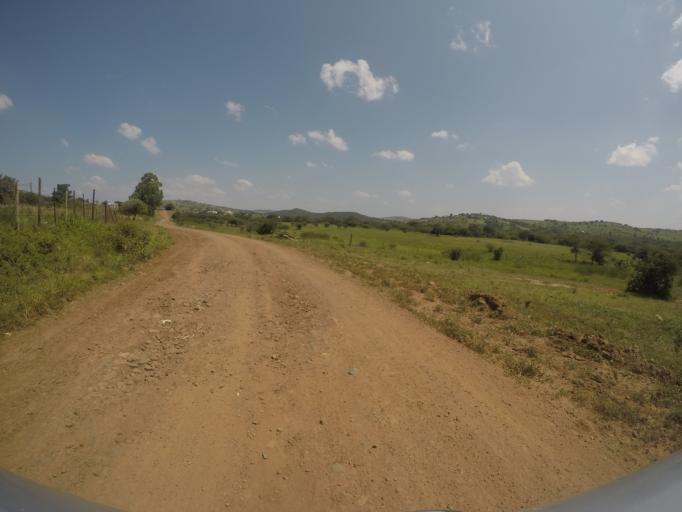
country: ZA
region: KwaZulu-Natal
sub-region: uThungulu District Municipality
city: Empangeni
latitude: -28.5885
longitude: 31.7371
